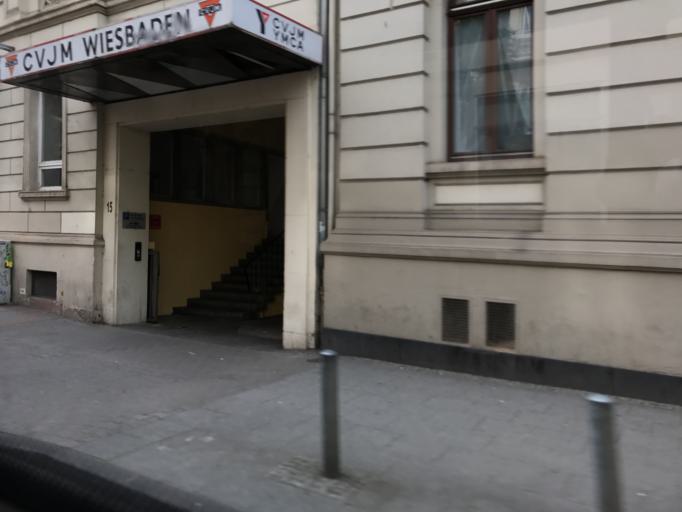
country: DE
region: Hesse
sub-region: Regierungsbezirk Darmstadt
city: Wiesbaden
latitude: 50.0759
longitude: 8.2370
